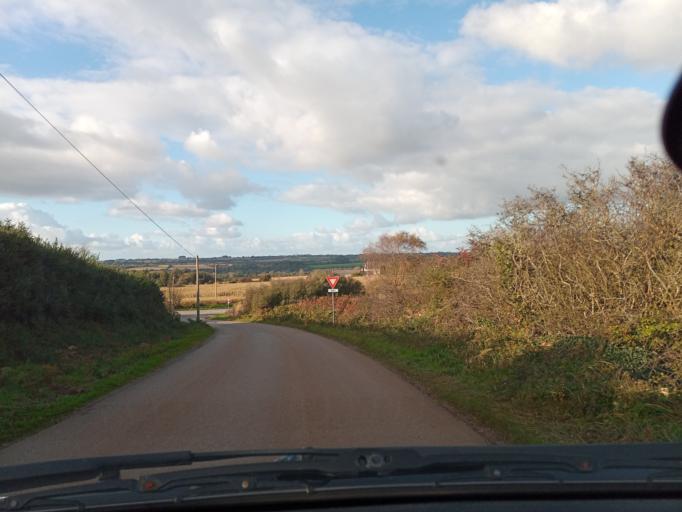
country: FR
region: Brittany
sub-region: Departement du Finistere
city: Plouhinec
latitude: 48.0278
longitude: -4.4984
